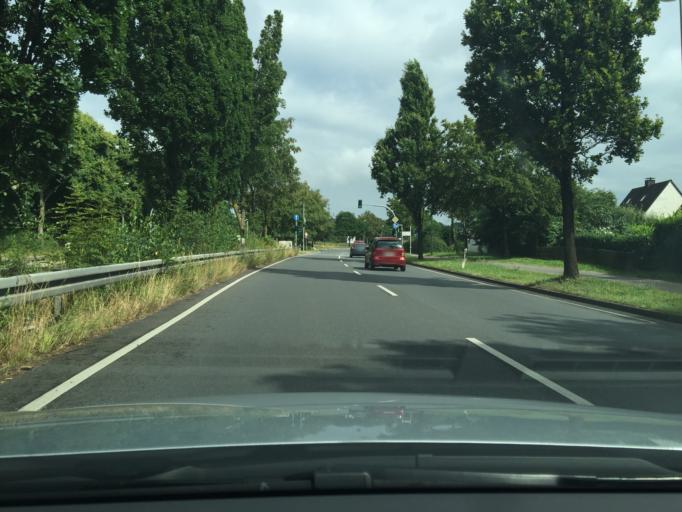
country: DE
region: North Rhine-Westphalia
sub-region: Regierungsbezirk Dusseldorf
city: Heiligenhaus
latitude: 51.3300
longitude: 6.9908
